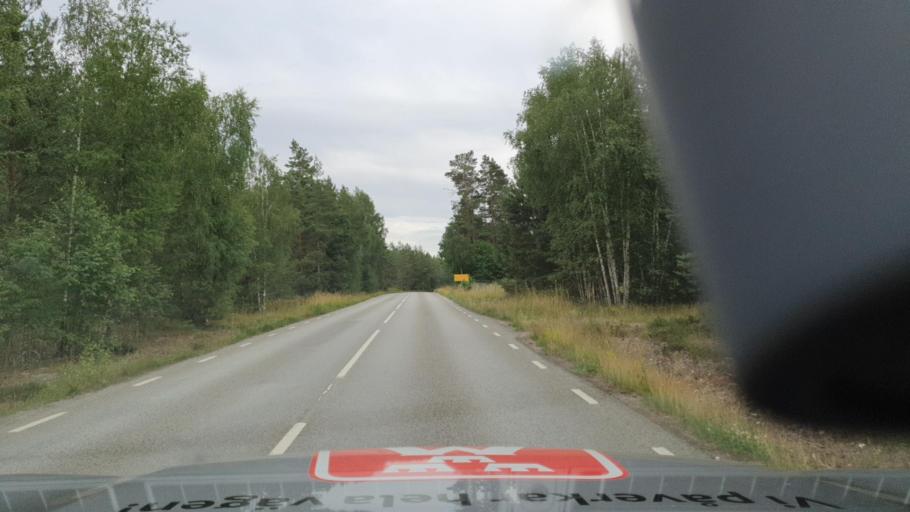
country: SE
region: Kalmar
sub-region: Kalmar Kommun
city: Trekanten
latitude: 56.6619
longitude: 16.0041
